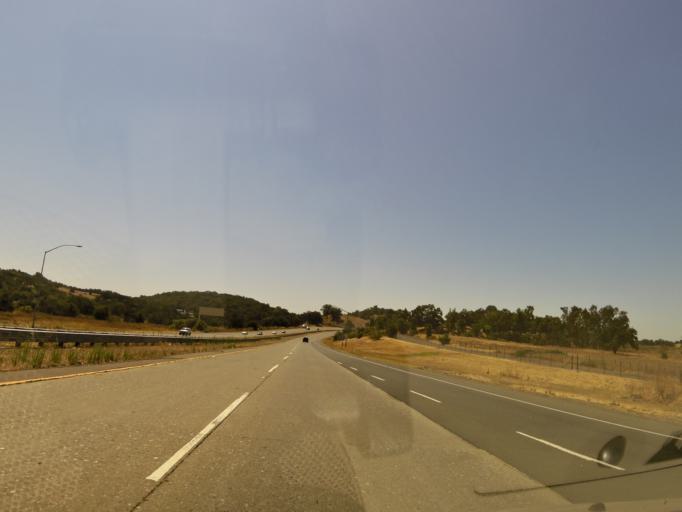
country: US
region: California
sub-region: Sonoma County
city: Healdsburg
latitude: 38.6568
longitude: -122.8736
